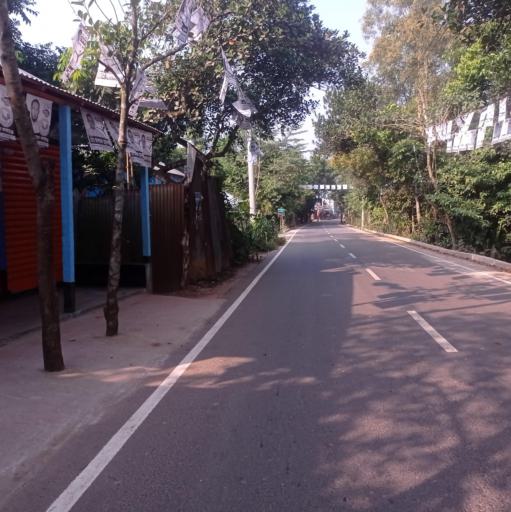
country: BD
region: Dhaka
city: Bhairab Bazar
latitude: 24.0445
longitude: 90.8348
